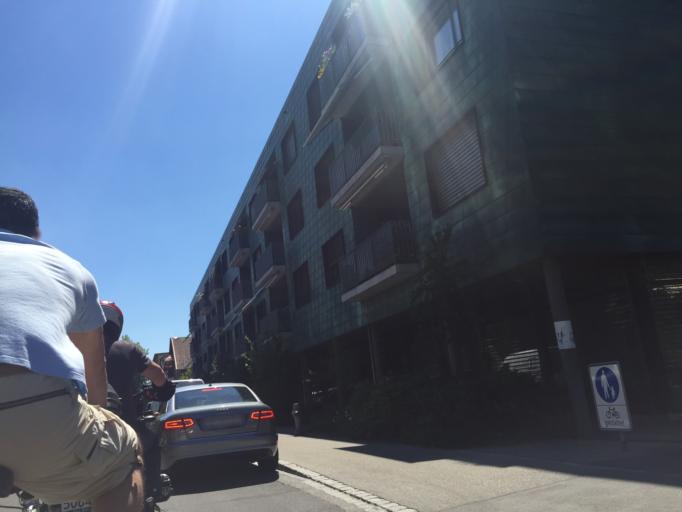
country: CH
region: Bern
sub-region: Bern-Mittelland District
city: Bern
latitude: 46.9545
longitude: 7.4249
